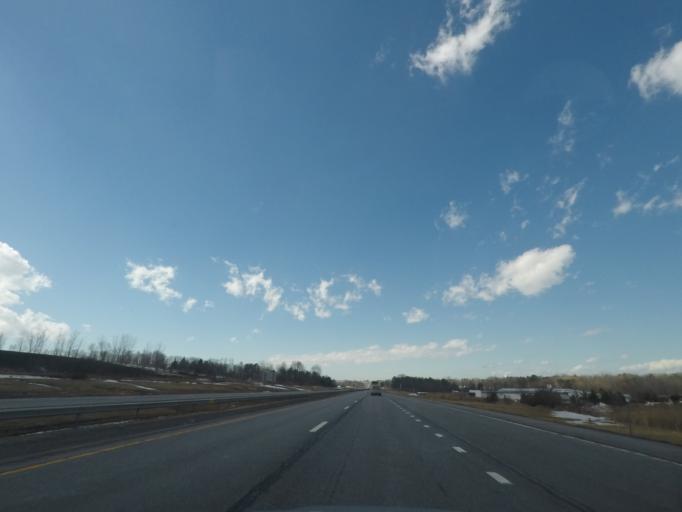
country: US
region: New York
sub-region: Montgomery County
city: Amsterdam
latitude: 42.9245
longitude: -74.2034
